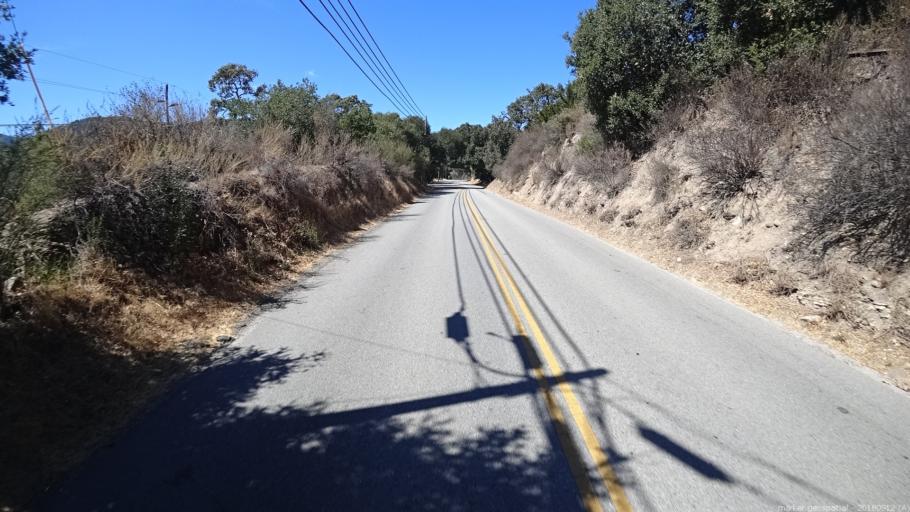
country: US
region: California
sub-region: Monterey County
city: Carmel Valley Village
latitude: 36.4761
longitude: -121.7209
